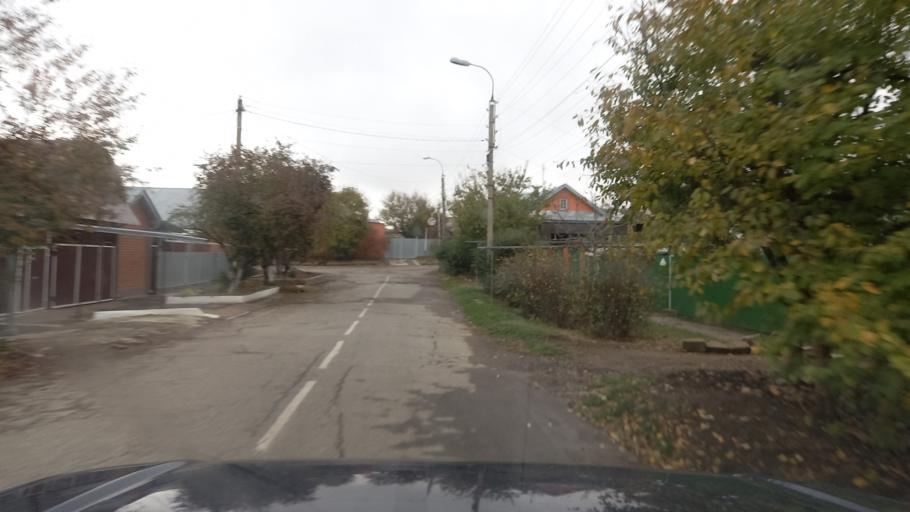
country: RU
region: Adygeya
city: Maykop
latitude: 44.6027
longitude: 40.0878
